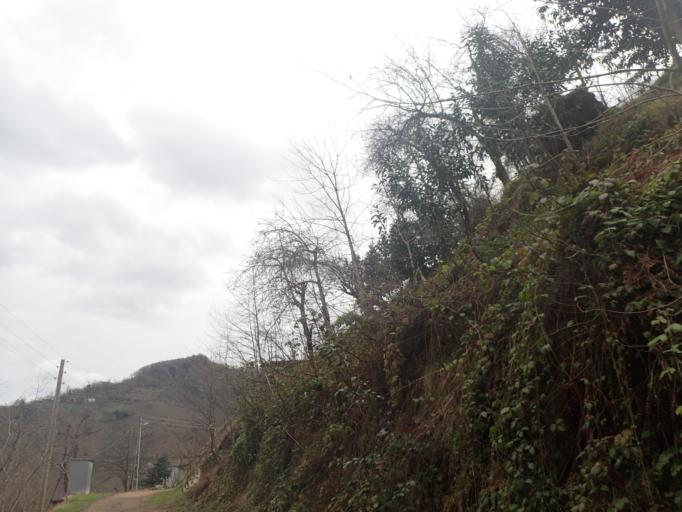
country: TR
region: Ordu
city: Camas
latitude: 40.9020
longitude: 37.5745
